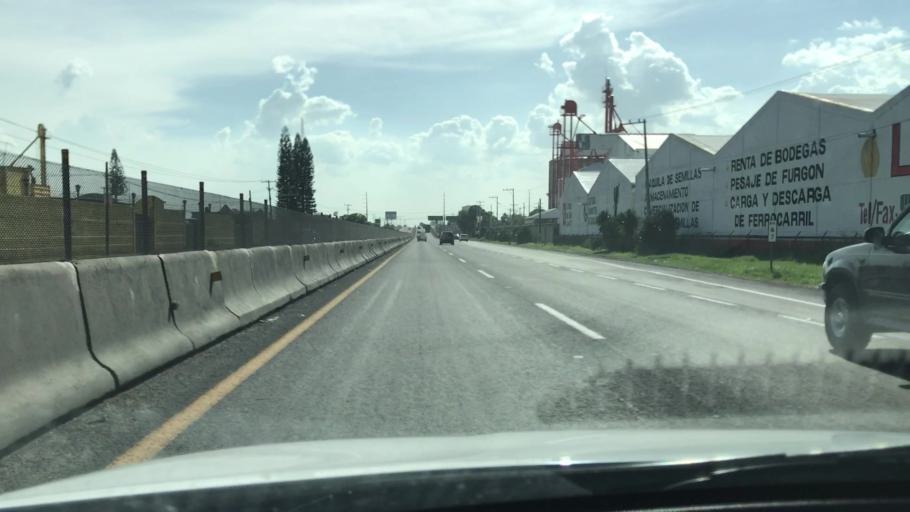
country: MX
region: Guanajuato
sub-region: Cortazar
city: Colonia la Calzada (La Olla)
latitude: 20.5116
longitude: -100.9481
